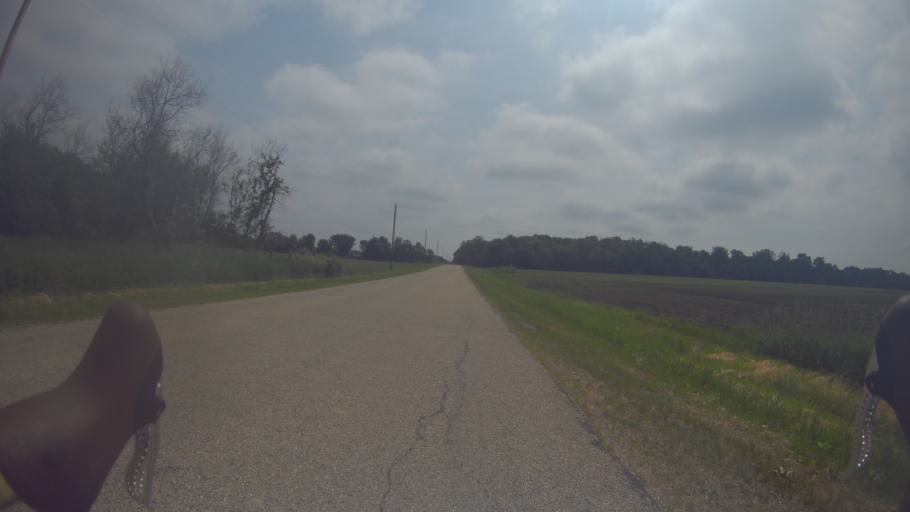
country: US
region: Wisconsin
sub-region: Jefferson County
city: Cambridge
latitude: 42.9232
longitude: -89.0214
